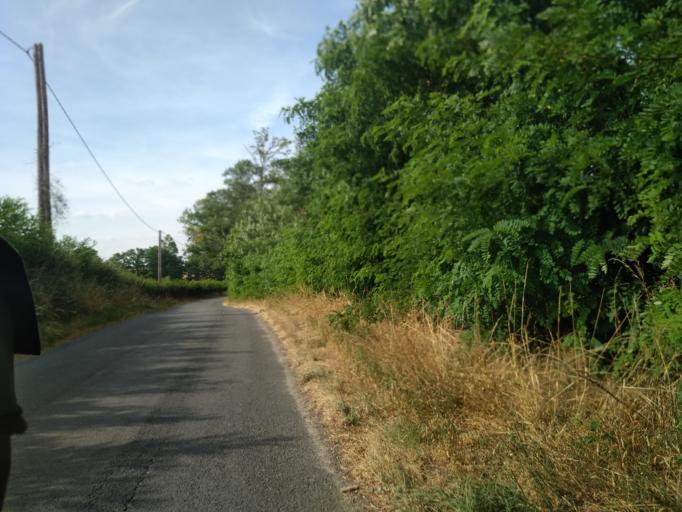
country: FR
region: Bourgogne
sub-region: Departement de Saone-et-Loire
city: Bourbon-Lancy
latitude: 46.6672
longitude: 3.7602
